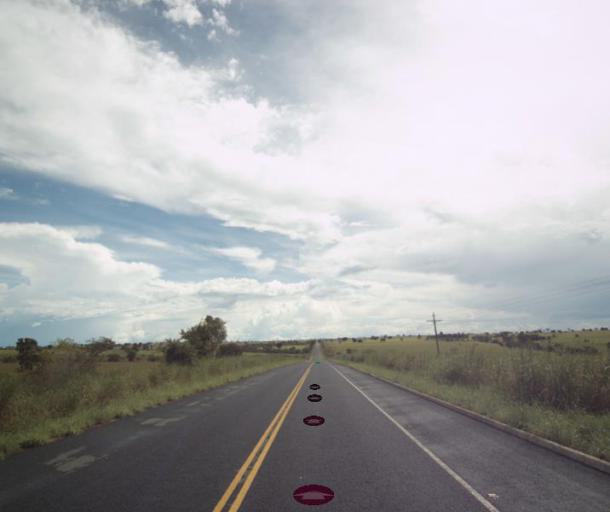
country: BR
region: Goias
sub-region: Sao Miguel Do Araguaia
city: Sao Miguel do Araguaia
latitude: -13.2922
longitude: -50.2192
